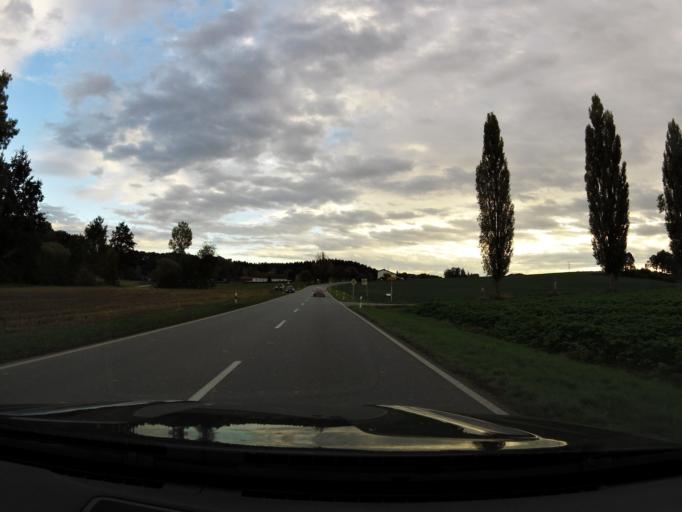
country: DE
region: Bavaria
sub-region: Lower Bavaria
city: Kumhausen
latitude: 48.4911
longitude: 12.1598
